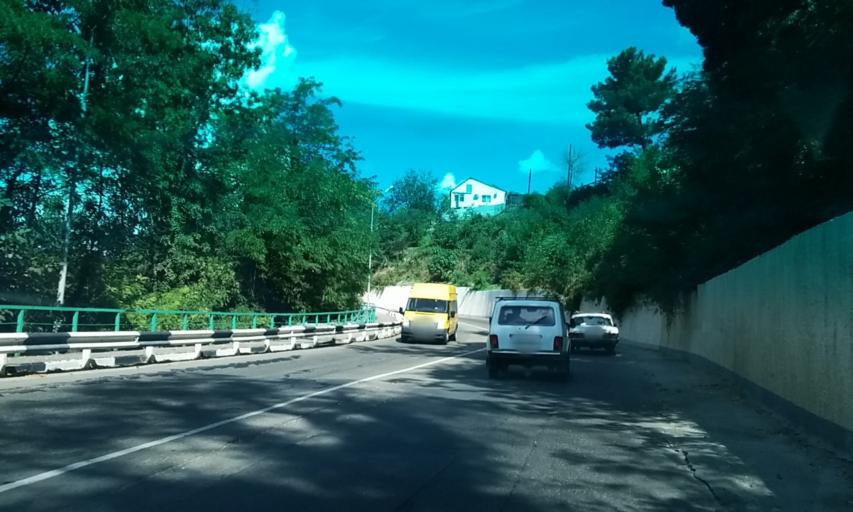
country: RU
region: Krasnodarskiy
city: Tuapse
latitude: 44.1016
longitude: 39.0645
